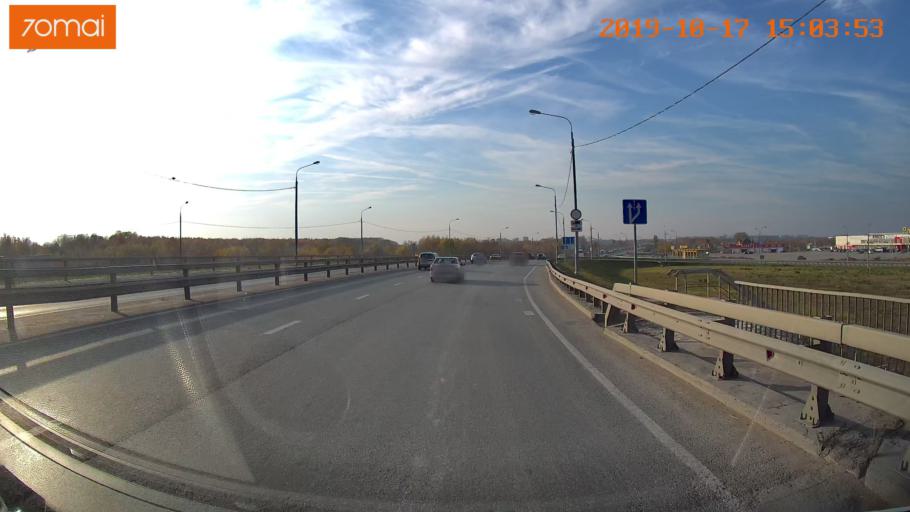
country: RU
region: Rjazan
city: Ryazan'
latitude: 54.6408
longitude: 39.7200
